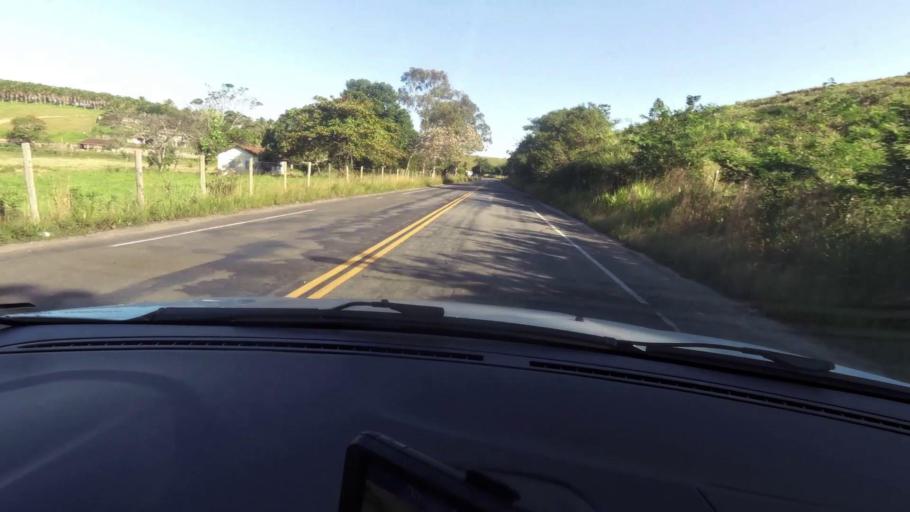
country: BR
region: Espirito Santo
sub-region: Piuma
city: Piuma
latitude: -20.7462
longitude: -40.6494
